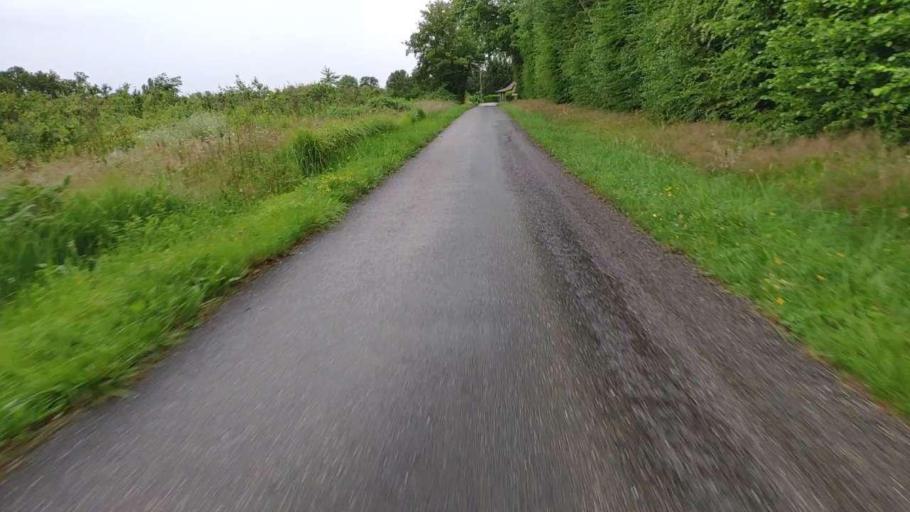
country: FR
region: Franche-Comte
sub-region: Departement du Jura
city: Chaussin
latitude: 46.8823
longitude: 5.4156
